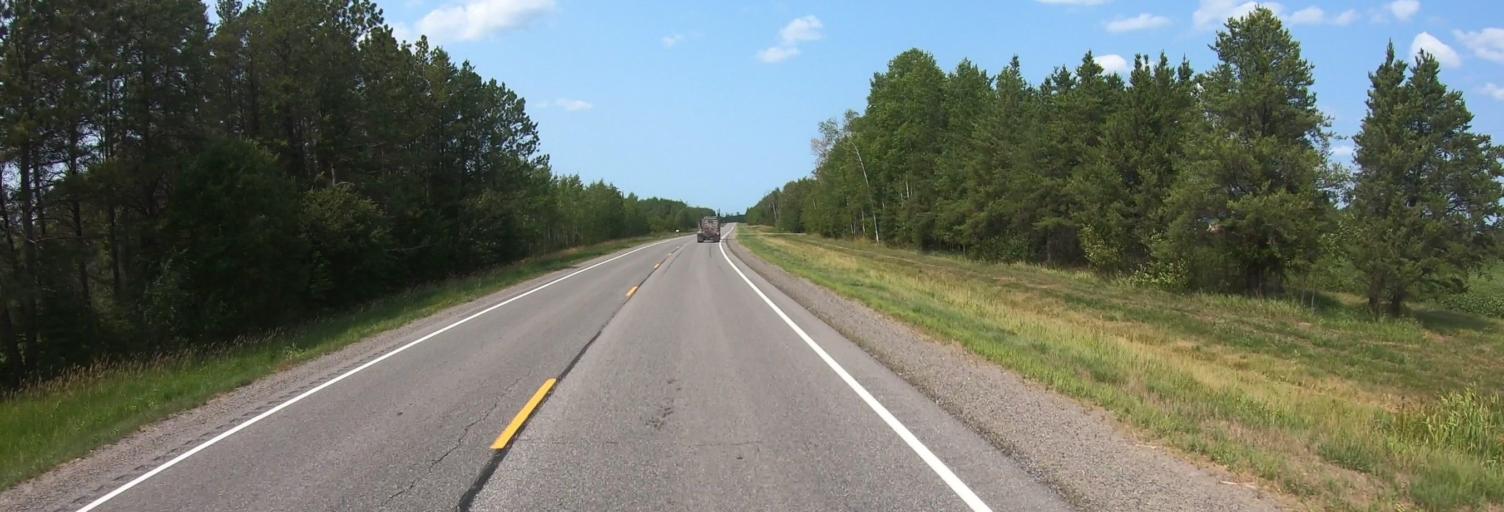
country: US
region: Minnesota
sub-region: Lake of the Woods County
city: Baudette
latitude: 48.6360
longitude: -94.1258
